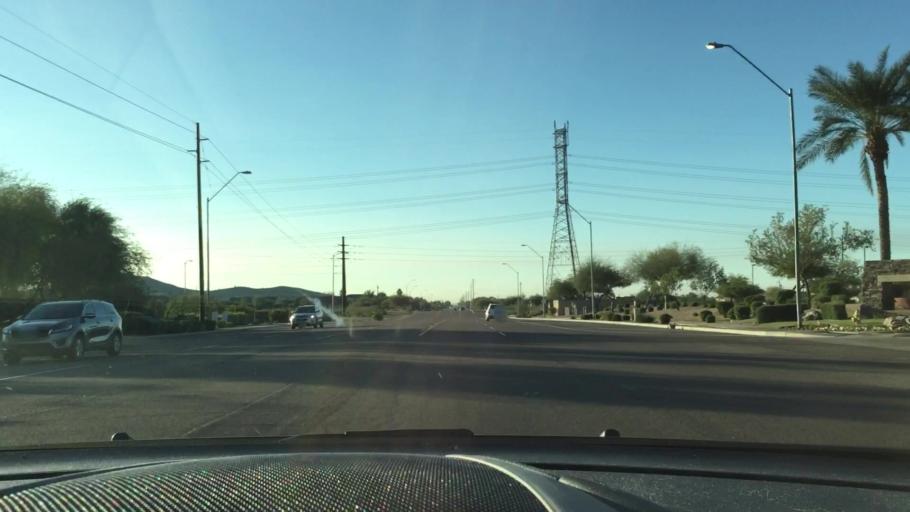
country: US
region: Arizona
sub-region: Maricopa County
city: Sun City
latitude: 33.7091
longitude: -112.2033
